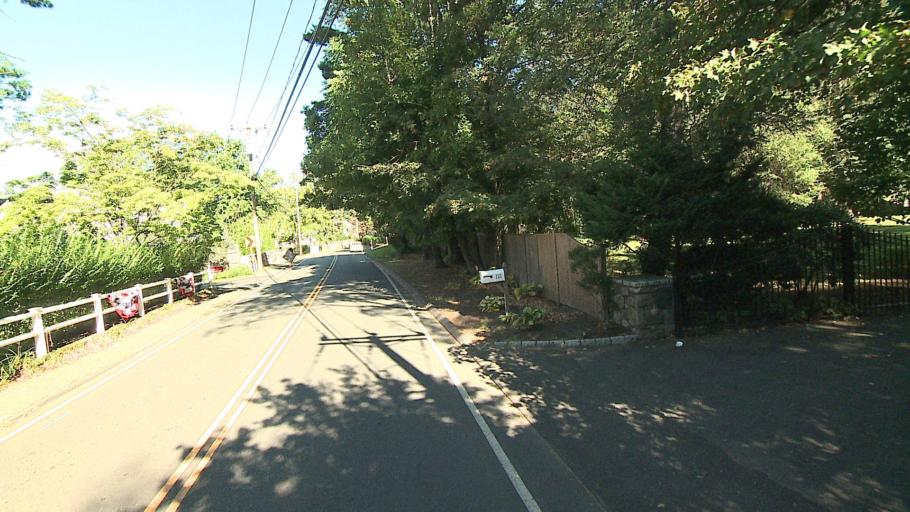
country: US
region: Connecticut
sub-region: Fairfield County
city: Stamford
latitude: 41.0871
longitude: -73.5122
